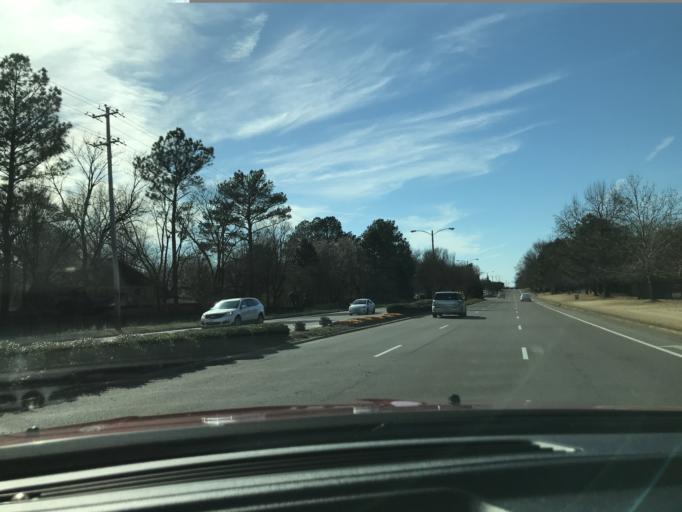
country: US
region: Tennessee
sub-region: Shelby County
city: Germantown
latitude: 35.0482
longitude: -89.7842
